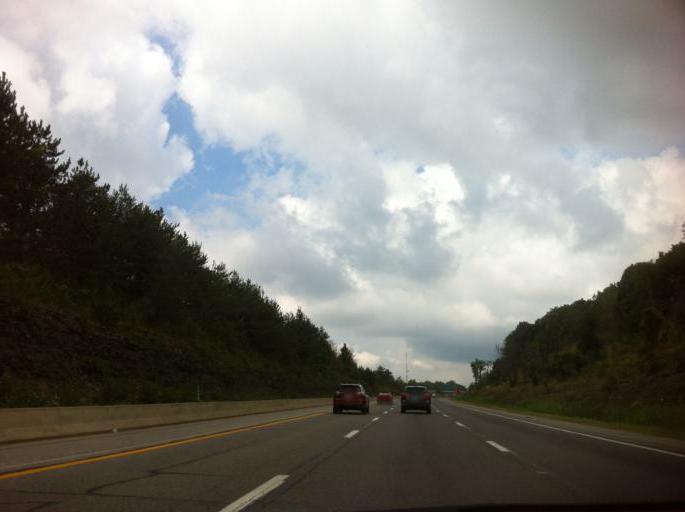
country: US
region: Ohio
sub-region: Summit County
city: Richfield
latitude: 41.2570
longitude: -81.5996
